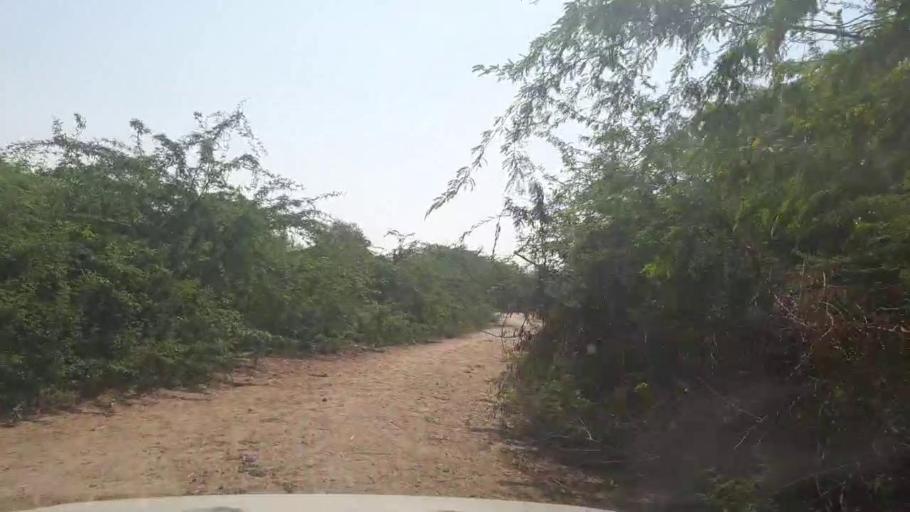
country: PK
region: Sindh
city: Chuhar Jamali
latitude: 24.3680
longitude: 67.8176
